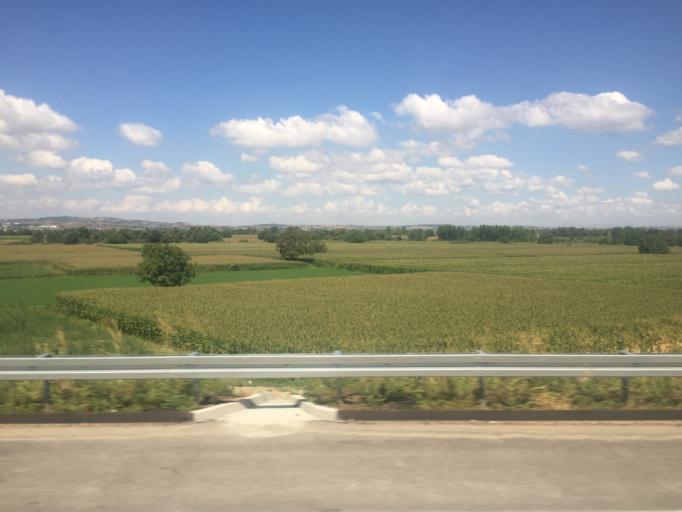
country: TR
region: Balikesir
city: Gobel
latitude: 40.0227
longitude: 28.2066
